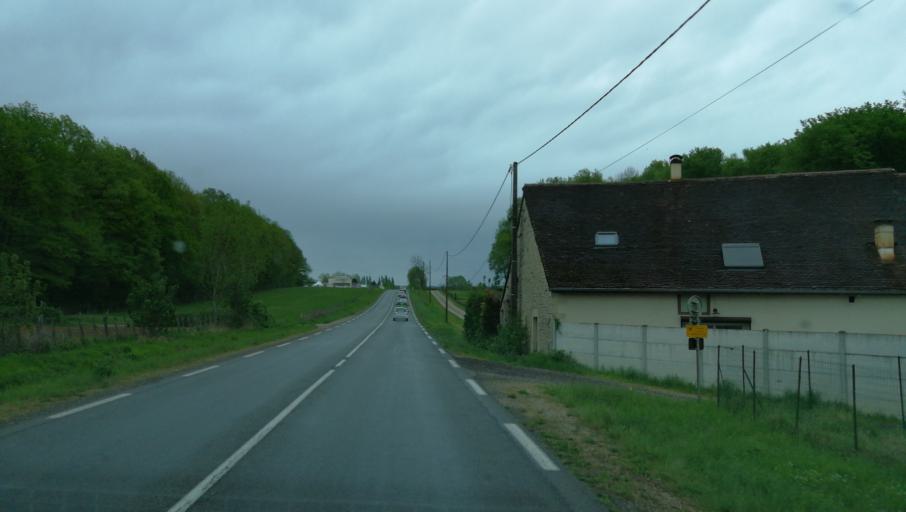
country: FR
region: Franche-Comte
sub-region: Departement du Jura
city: Montmorot
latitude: 46.6925
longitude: 5.4974
